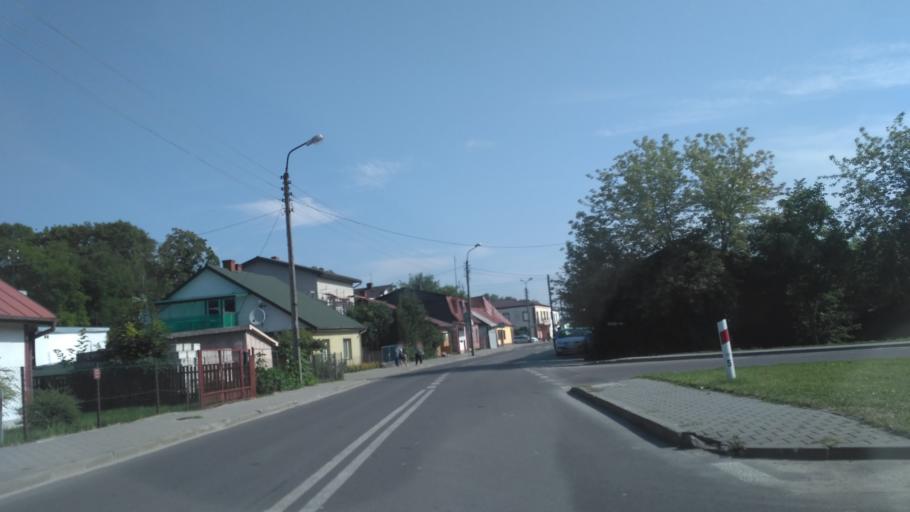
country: PL
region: Lublin Voivodeship
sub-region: Powiat leczynski
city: Cycow
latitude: 51.1935
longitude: 23.1634
